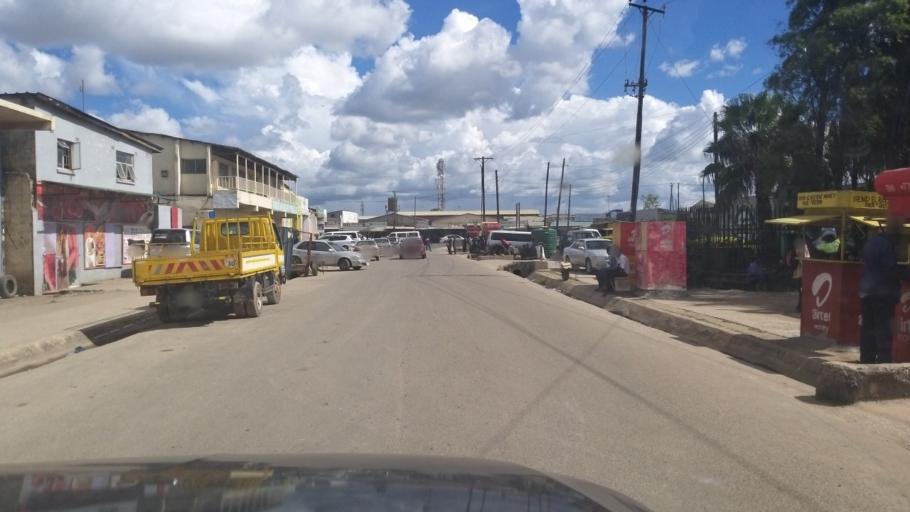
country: ZM
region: Lusaka
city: Lusaka
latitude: -15.4151
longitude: 28.2744
